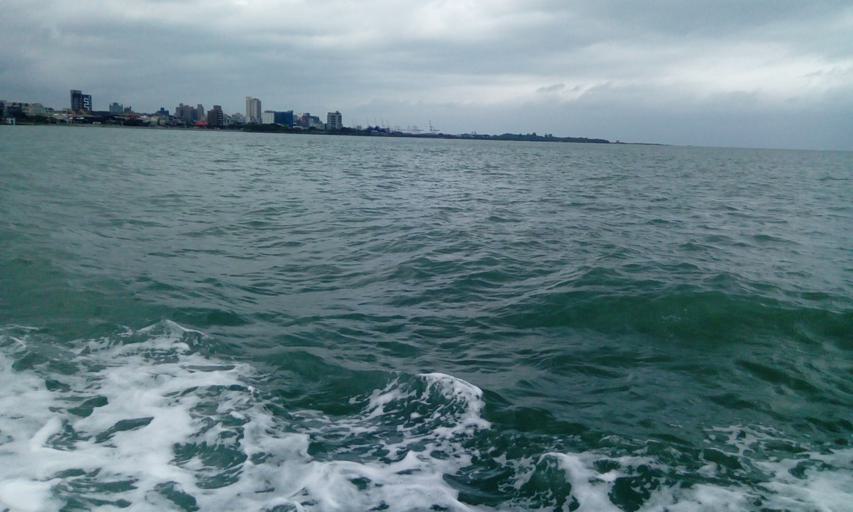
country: TW
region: Taipei
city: Taipei
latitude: 25.1642
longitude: 121.4368
